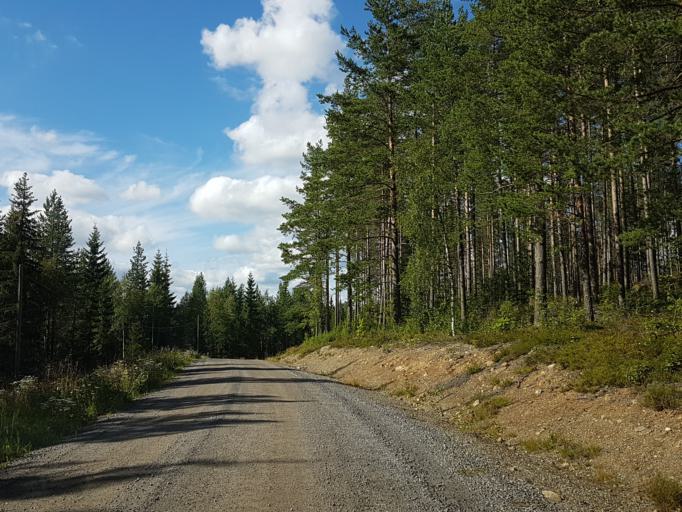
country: SE
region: Vaesterbotten
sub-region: Skelleftea Kommun
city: Burtraesk
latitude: 64.2737
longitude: 20.4828
